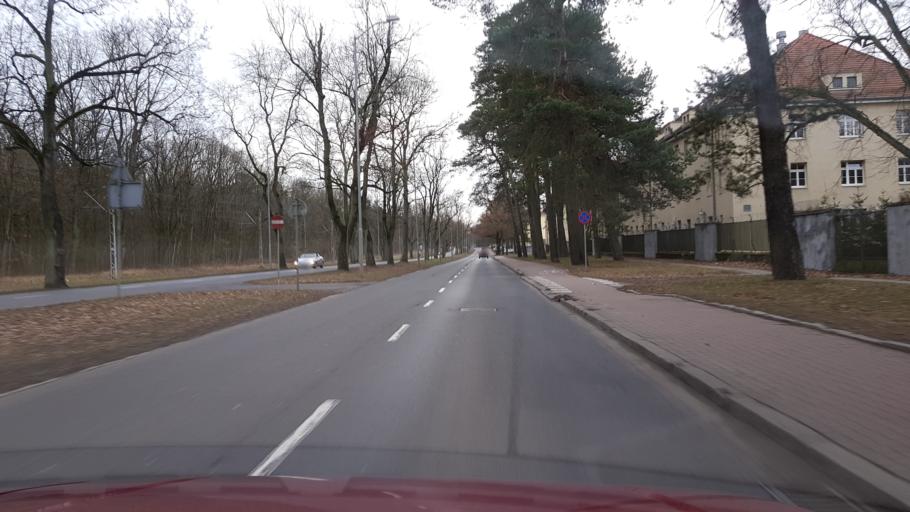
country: PL
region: West Pomeranian Voivodeship
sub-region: Szczecin
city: Szczecin
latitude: 53.4665
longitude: 14.4907
